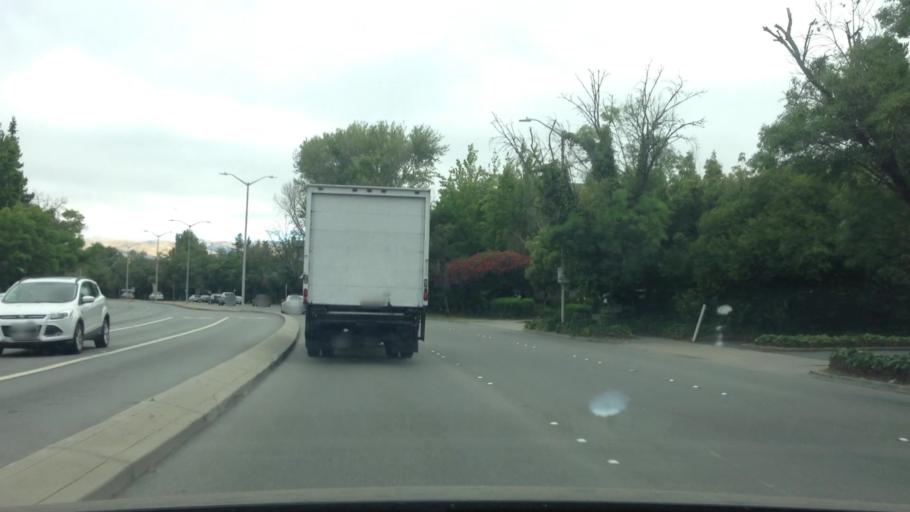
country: US
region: California
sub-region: Alameda County
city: Fremont
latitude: 37.5409
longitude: -121.9729
